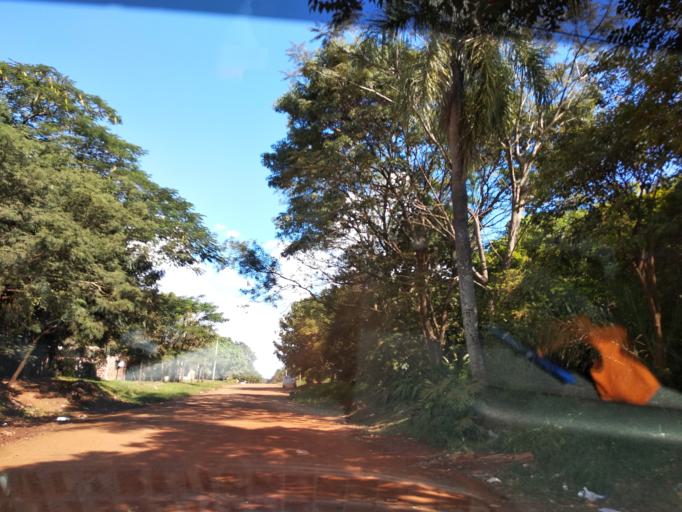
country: AR
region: Misiones
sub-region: Departamento de Capital
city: Posadas
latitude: -27.3728
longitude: -55.9439
